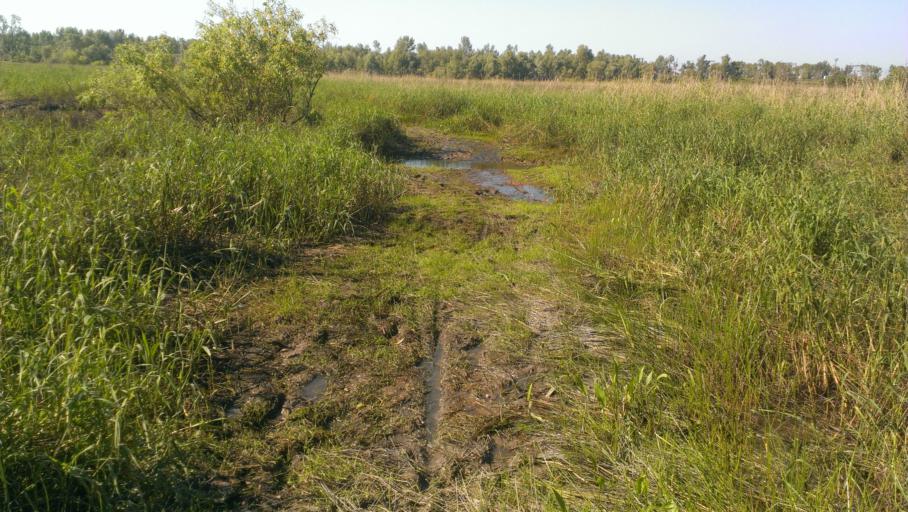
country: RU
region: Altai Krai
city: Novoaltaysk
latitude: 53.3649
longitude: 83.8616
